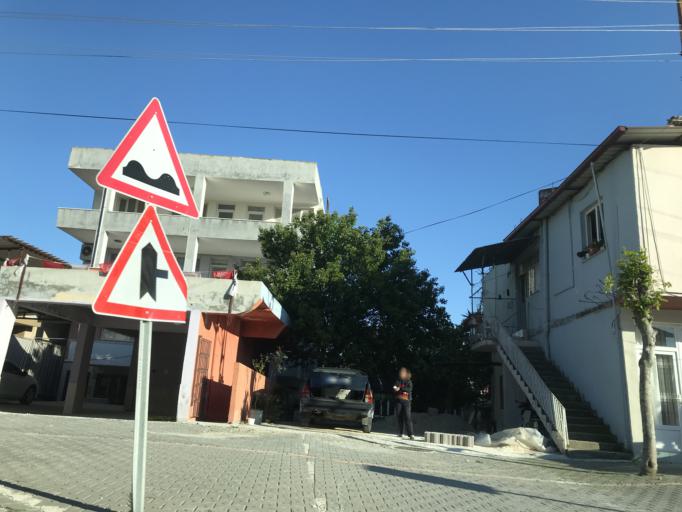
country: TR
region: Hatay
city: Samandag
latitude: 36.0848
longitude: 35.9660
